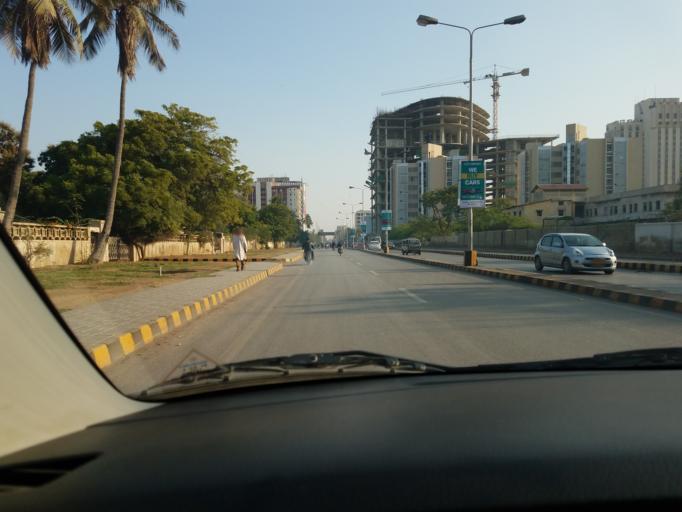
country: PK
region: Sindh
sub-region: Karachi District
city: Karachi
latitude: 24.8558
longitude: 67.0326
